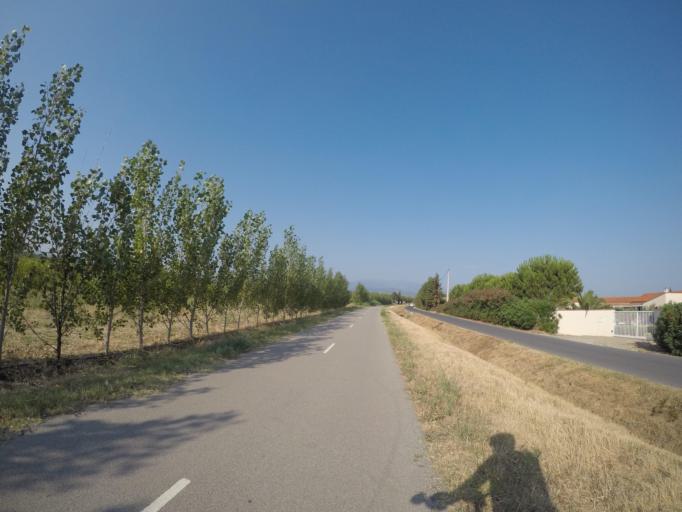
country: FR
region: Languedoc-Roussillon
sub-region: Departement des Pyrenees-Orientales
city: Ponteilla
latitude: 42.6237
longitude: 2.7976
